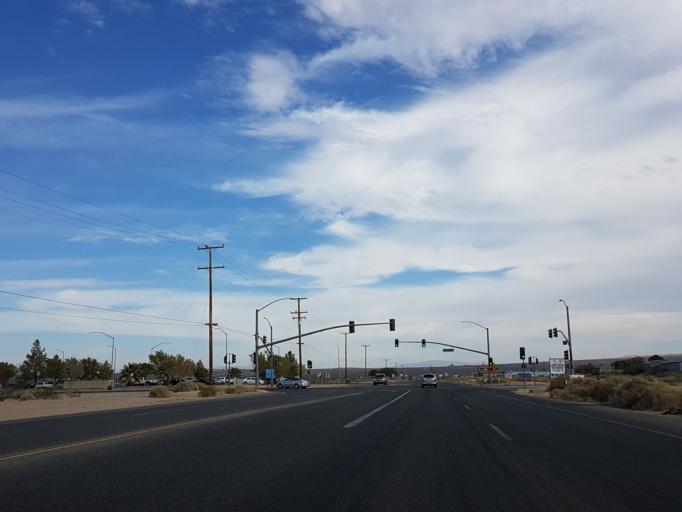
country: US
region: California
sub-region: Kern County
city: Ridgecrest
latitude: 35.6225
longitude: -117.6491
